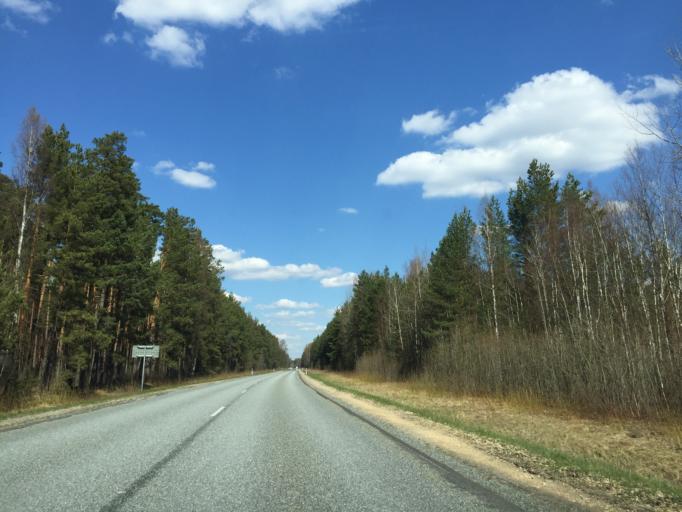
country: LV
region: Saulkrastu
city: Saulkrasti
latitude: 57.2148
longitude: 24.3832
